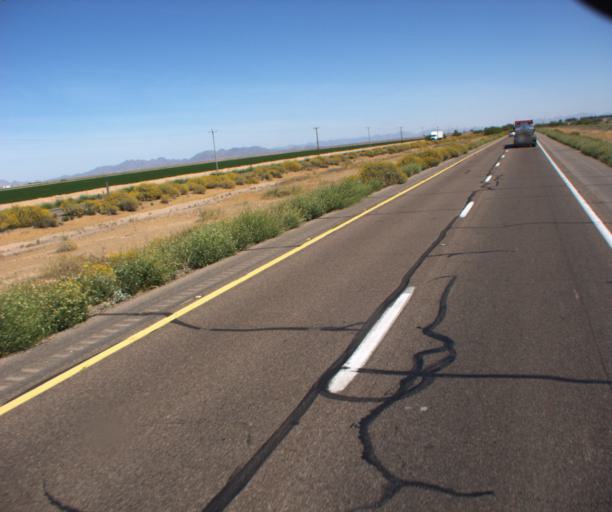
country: US
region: Arizona
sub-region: Maricopa County
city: Gila Bend
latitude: 32.9151
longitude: -112.9309
